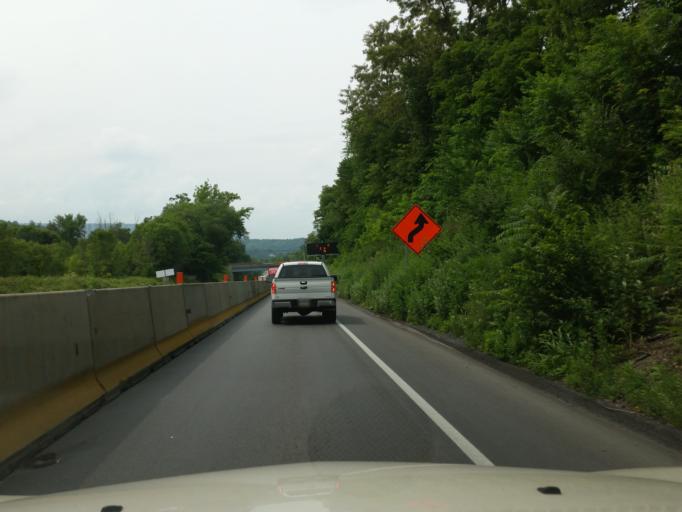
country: US
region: Pennsylvania
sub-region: Mifflin County
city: Lewistown
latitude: 40.5972
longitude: -77.5598
